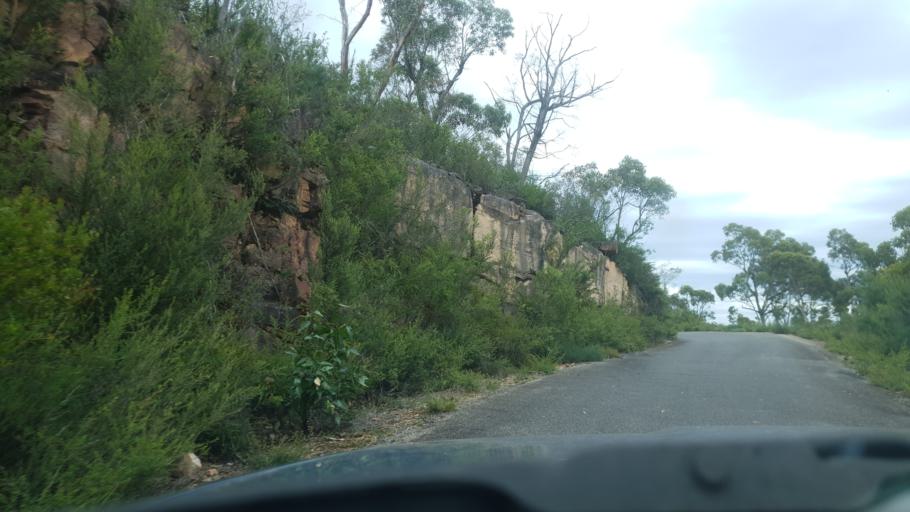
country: AU
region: Victoria
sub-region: Northern Grampians
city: Stawell
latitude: -37.2656
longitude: 142.5781
